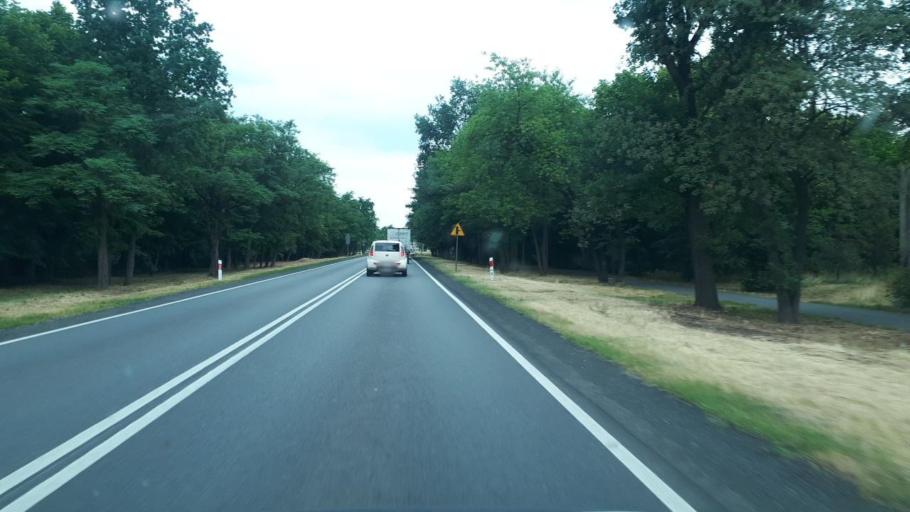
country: PL
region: Greater Poland Voivodeship
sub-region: Powiat ostrzeszowski
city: Ostrzeszow
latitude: 51.4323
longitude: 17.9178
